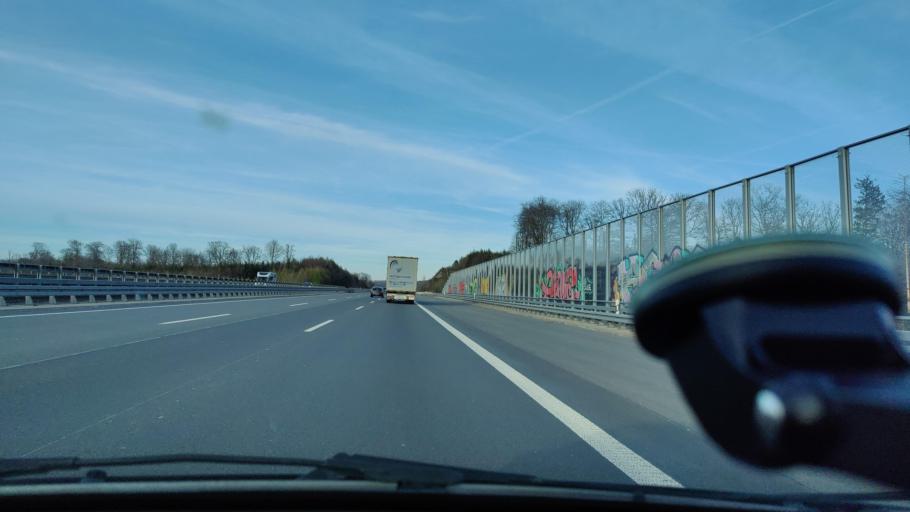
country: DE
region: North Rhine-Westphalia
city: Wermelskirchen
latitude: 51.1526
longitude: 7.2121
